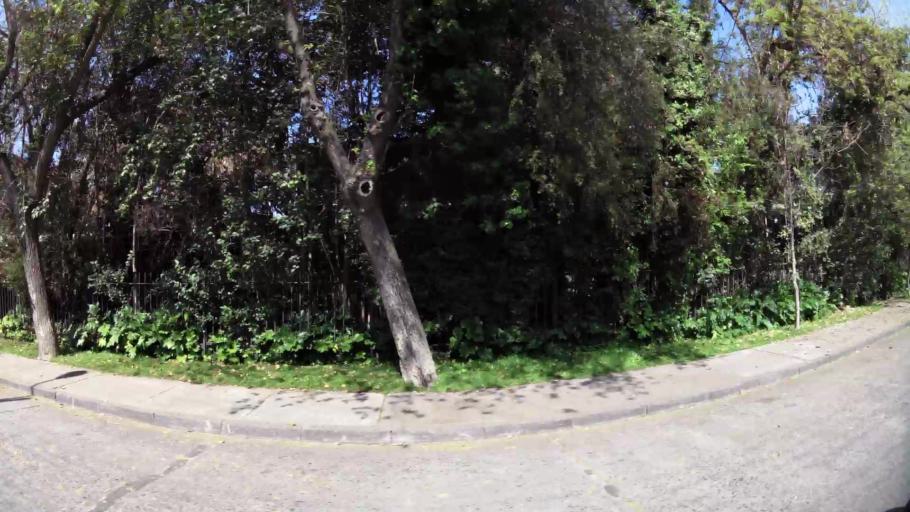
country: CL
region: Santiago Metropolitan
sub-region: Provincia de Santiago
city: Santiago
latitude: -33.4191
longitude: -70.6187
